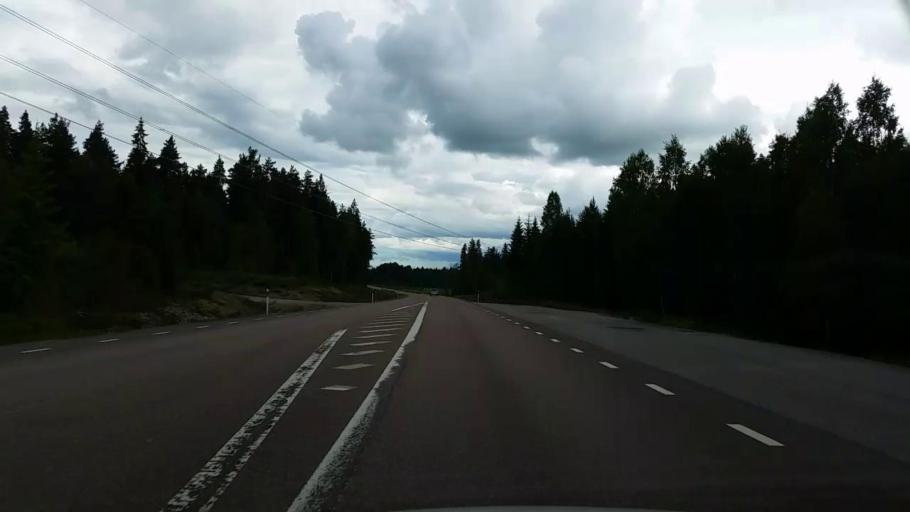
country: SE
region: Dalarna
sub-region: Avesta Kommun
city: Horndal
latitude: 60.4714
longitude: 16.4486
